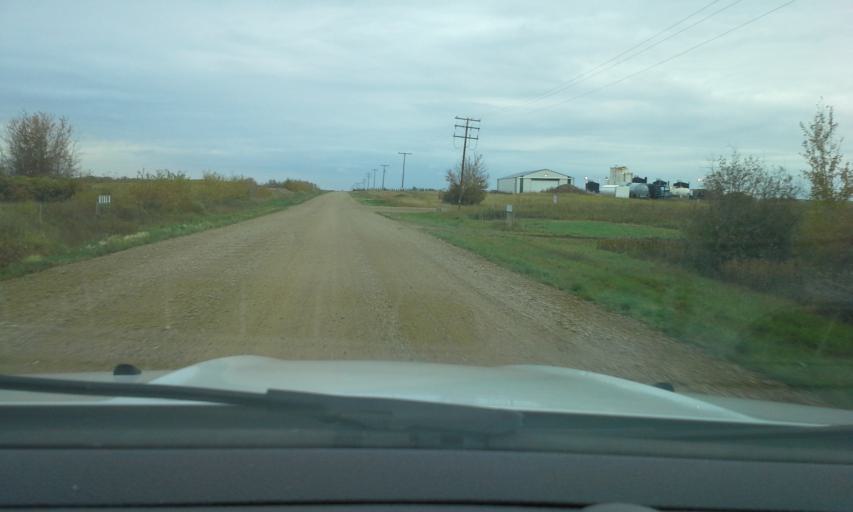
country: CA
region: Saskatchewan
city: Lloydminster
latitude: 53.2927
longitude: -109.8085
